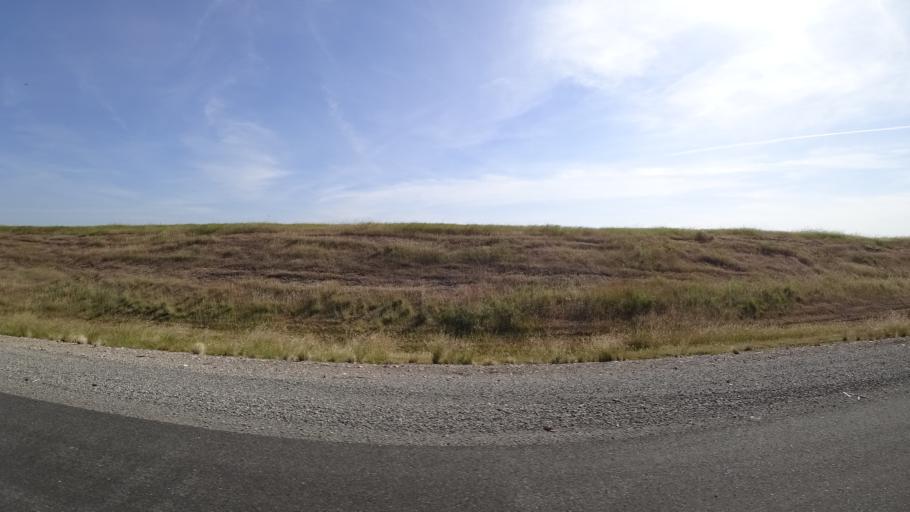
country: US
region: California
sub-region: Butte County
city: Thermalito
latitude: 39.5956
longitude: -121.6500
